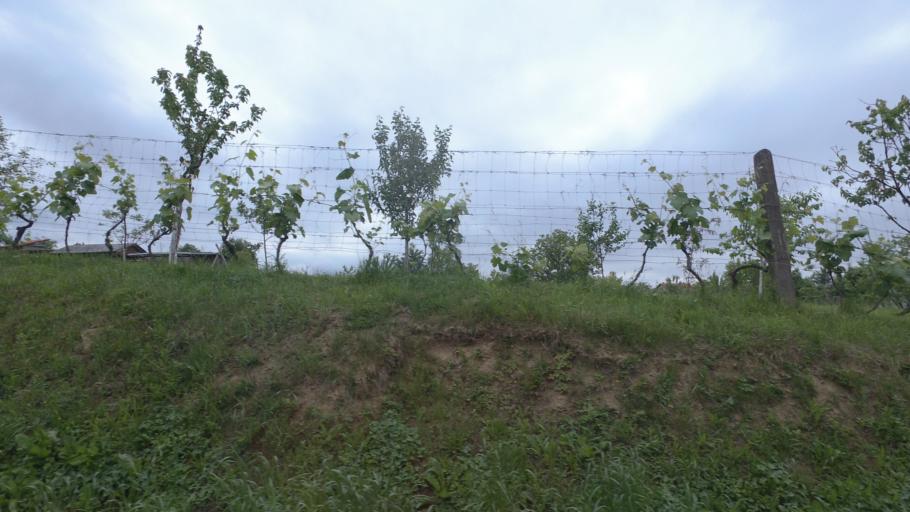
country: HR
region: Karlovacka
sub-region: Grad Karlovac
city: Karlovac
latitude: 45.4339
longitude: 15.5572
